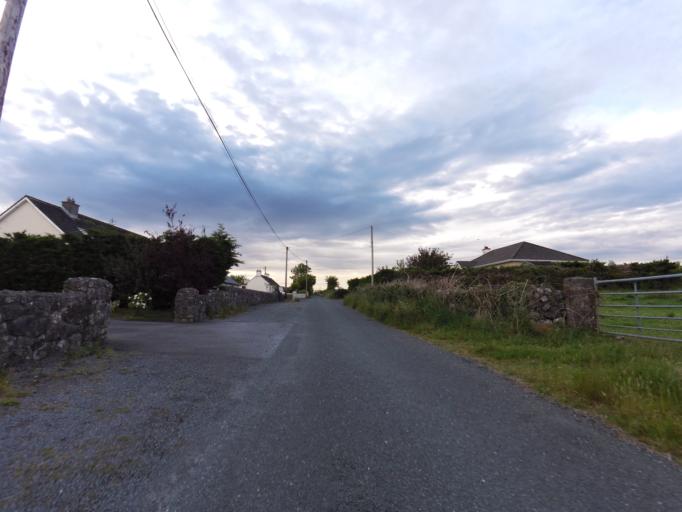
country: IE
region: Connaught
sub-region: County Galway
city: Athenry
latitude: 53.2889
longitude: -8.7142
